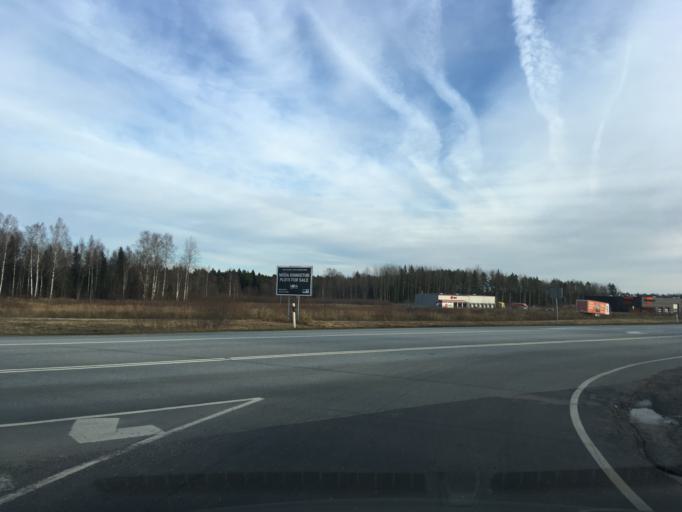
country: EE
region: Ida-Virumaa
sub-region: Johvi vald
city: Johvi
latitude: 59.3681
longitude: 27.4174
